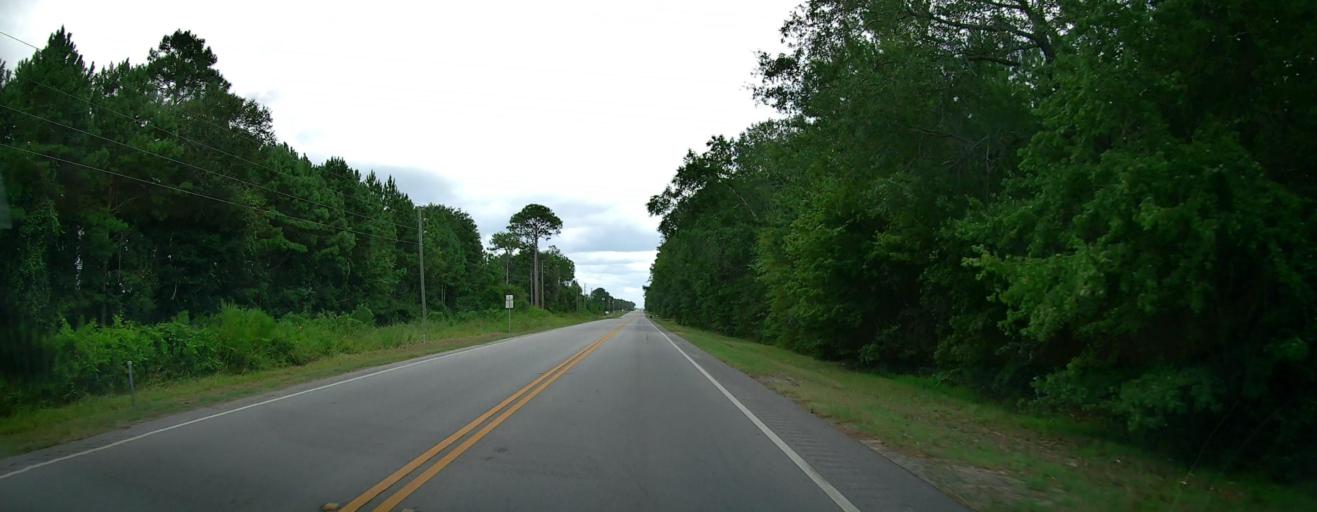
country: US
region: Georgia
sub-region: Coffee County
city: Broxton
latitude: 31.5716
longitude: -83.0271
